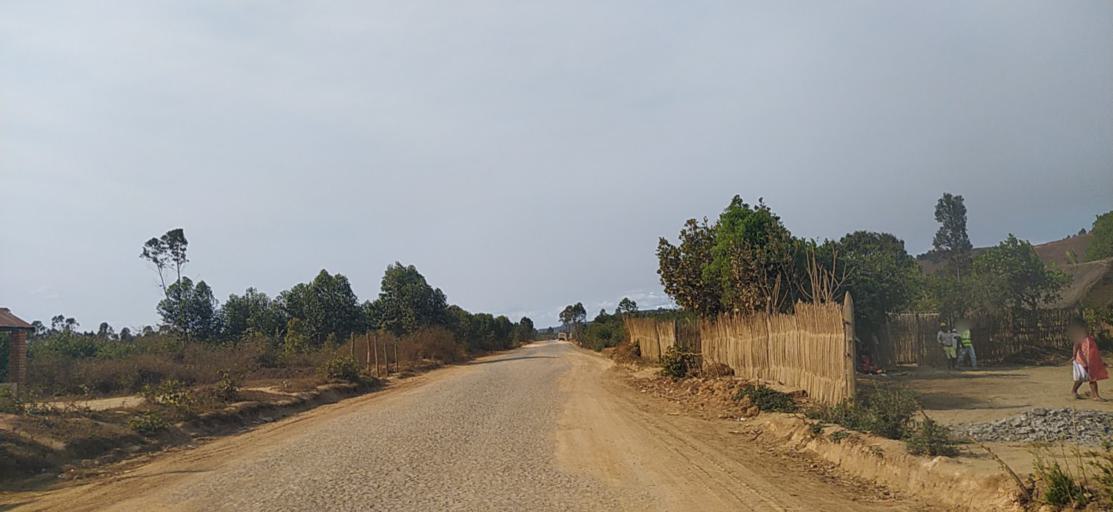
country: MG
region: Alaotra Mangoro
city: Moramanga
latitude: -18.6732
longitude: 48.2734
